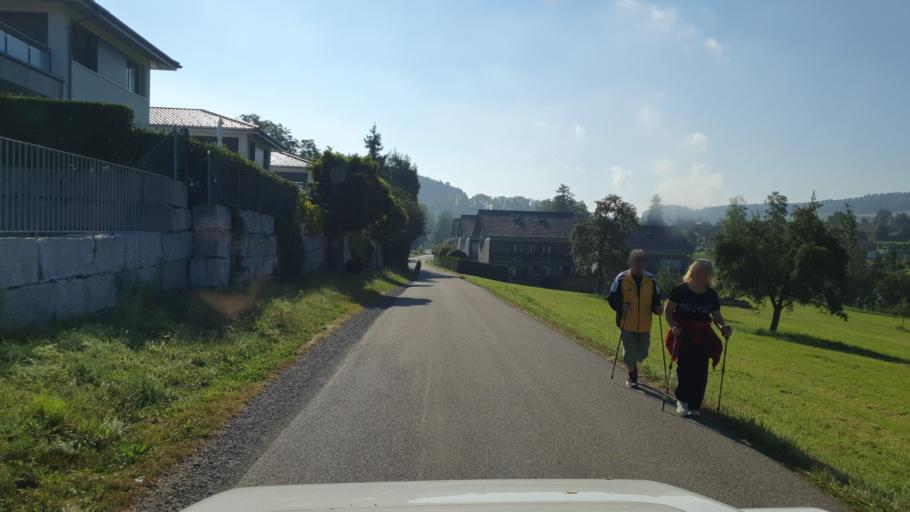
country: CH
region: Aargau
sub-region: Bezirk Bremgarten
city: Sarmenstorf
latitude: 47.3297
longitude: 8.2644
